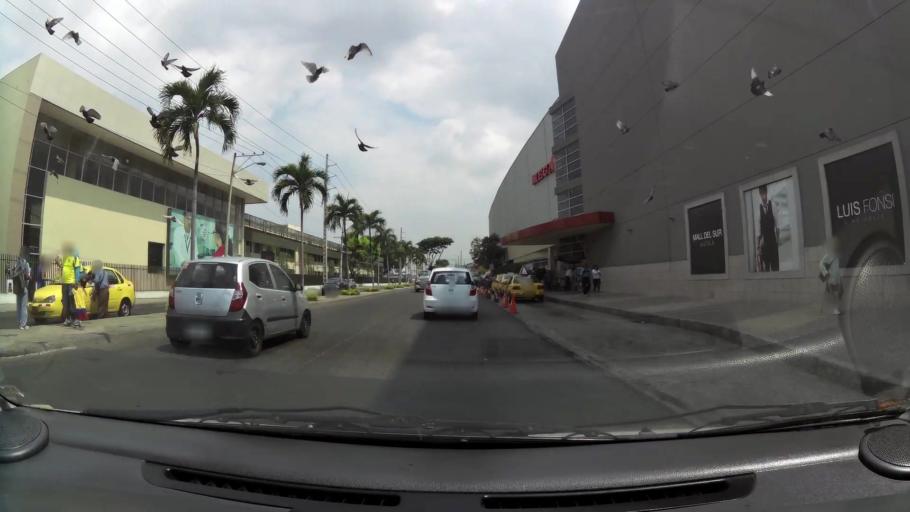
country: EC
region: Guayas
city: Guayaquil
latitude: -2.2304
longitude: -79.8981
